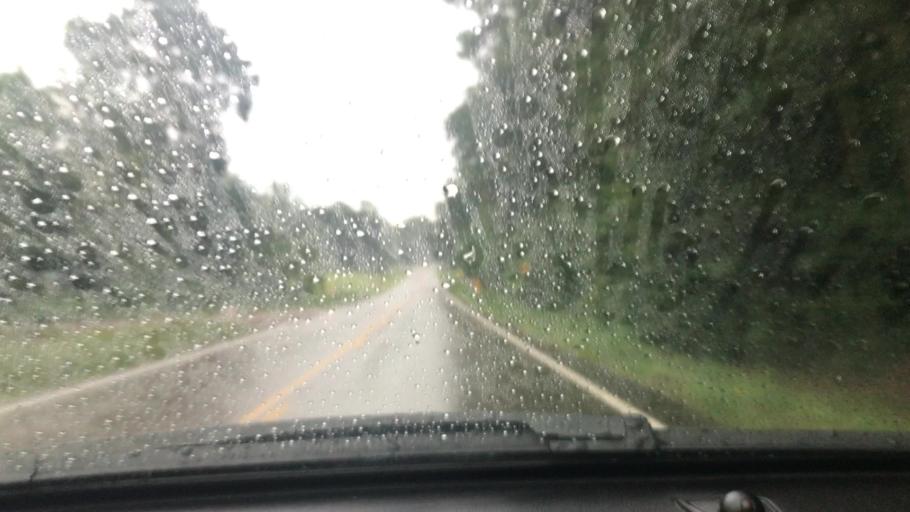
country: US
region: Mississippi
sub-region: Pike County
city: Summit
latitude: 31.3186
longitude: -90.5319
